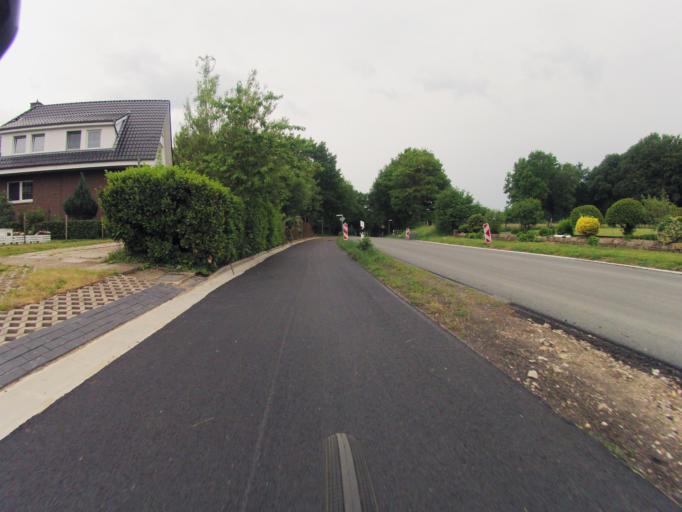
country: DE
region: North Rhine-Westphalia
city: Ibbenburen
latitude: 52.3097
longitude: 7.6701
